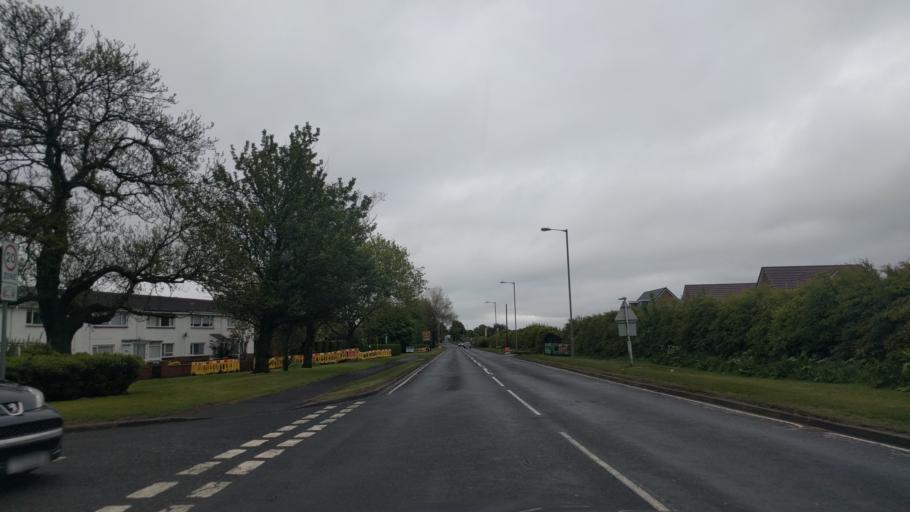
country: GB
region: England
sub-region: Northumberland
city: Morpeth
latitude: 55.1573
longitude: -1.6740
